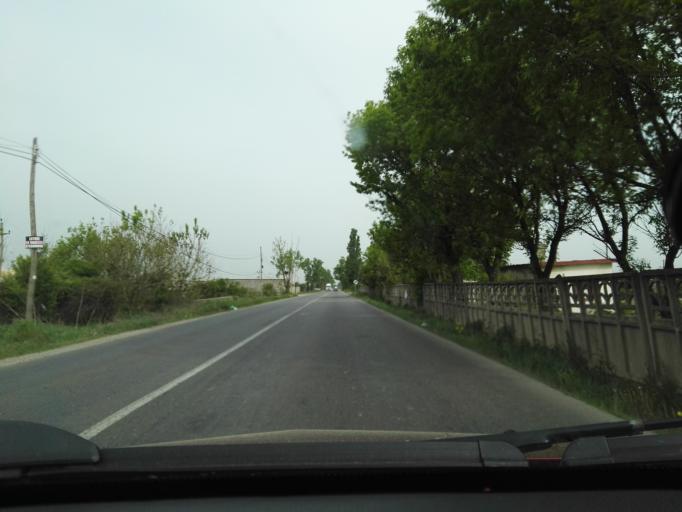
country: RO
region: Ilfov
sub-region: Comuna Magurele
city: Magurele
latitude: 44.3672
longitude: 26.0166
